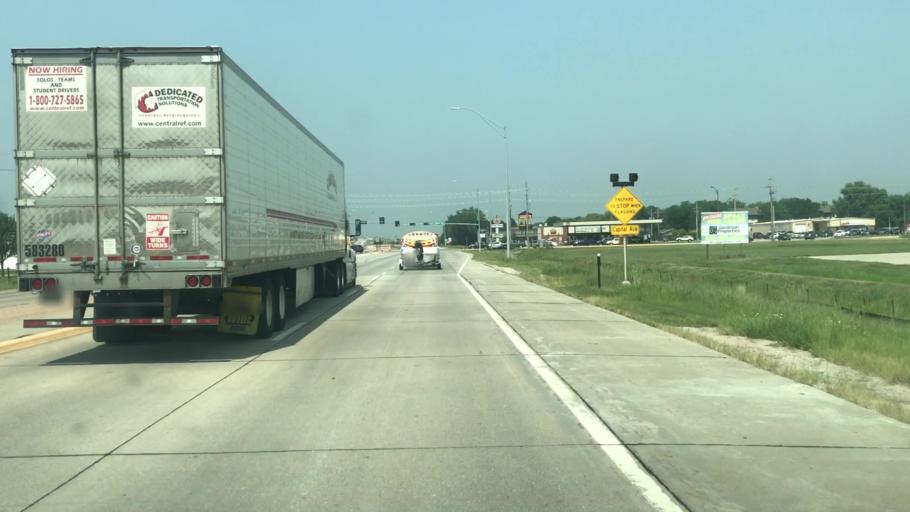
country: US
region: Nebraska
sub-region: Hall County
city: Grand Island
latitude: 40.9442
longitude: -98.3835
